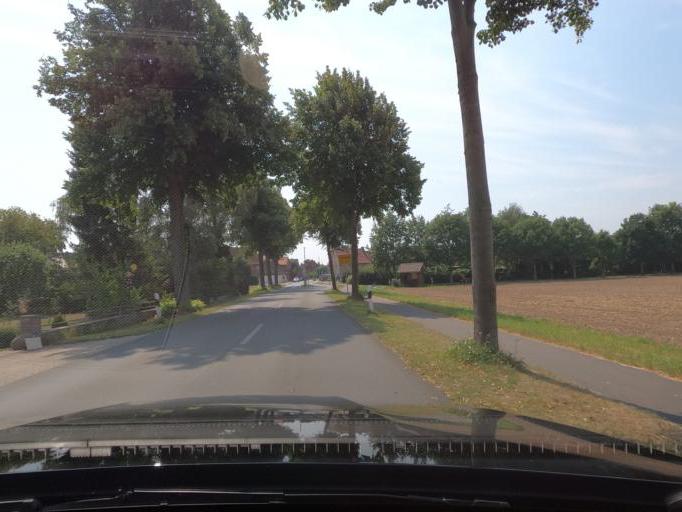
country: DE
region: Lower Saxony
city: Sarstedt
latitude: 52.2397
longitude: 9.8210
